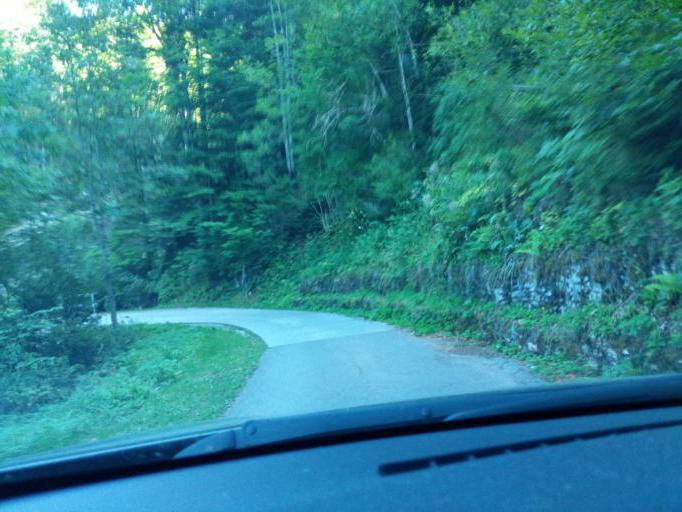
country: CH
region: Bern
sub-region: Obersimmental-Saanen District
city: Zweisimmen
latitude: 46.6083
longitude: 7.2805
